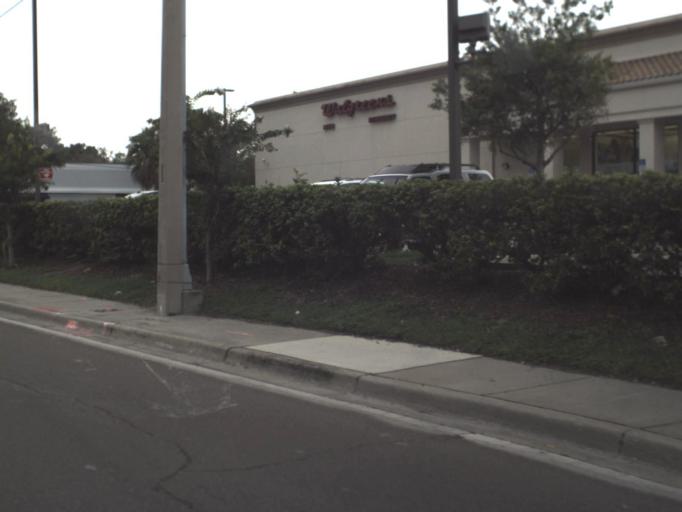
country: US
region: Florida
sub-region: Sarasota County
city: South Sarasota
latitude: 27.2988
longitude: -82.5302
